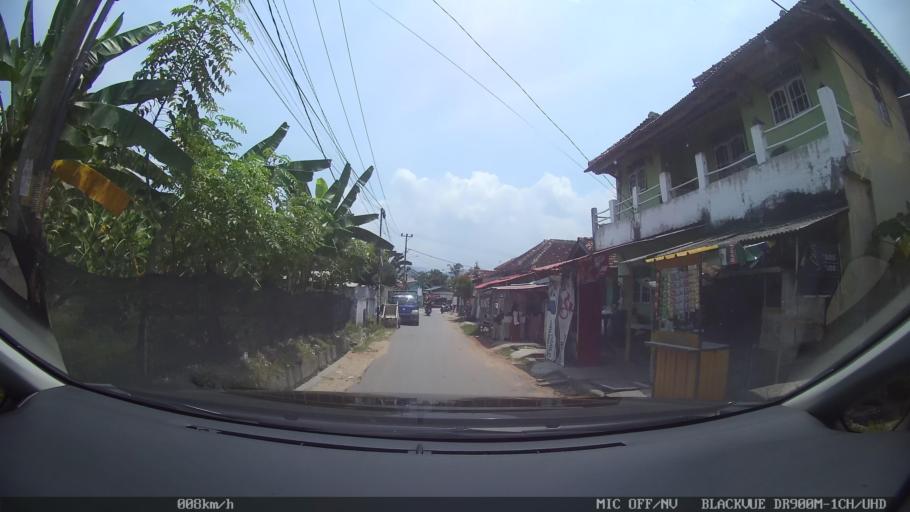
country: ID
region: Lampung
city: Bandarlampung
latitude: -5.4590
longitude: 105.2585
